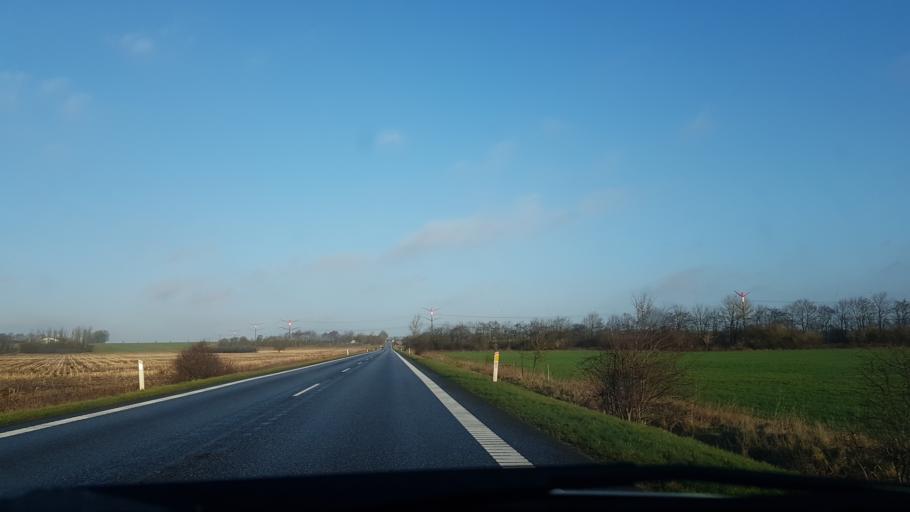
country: DK
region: South Denmark
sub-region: Tonder Kommune
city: Toftlund
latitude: 55.2435
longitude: 9.1337
